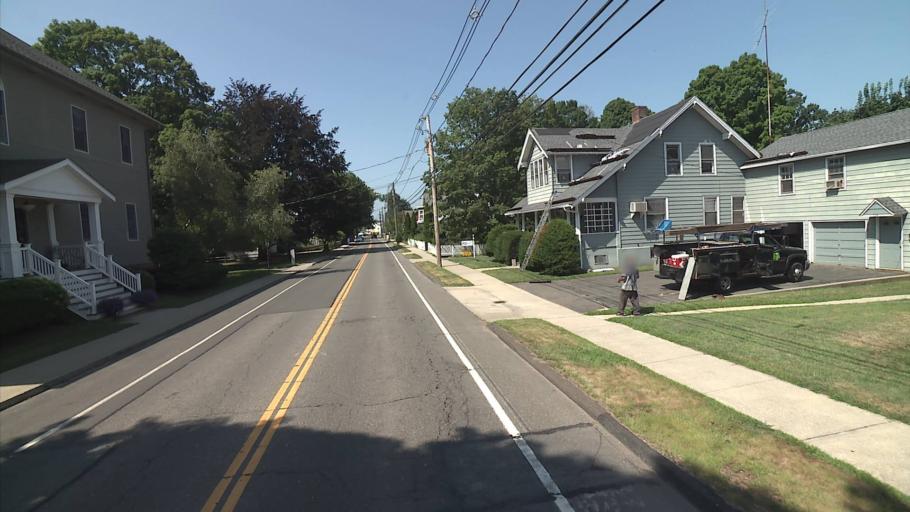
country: US
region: Connecticut
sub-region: New Haven County
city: Guilford Center
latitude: 41.2829
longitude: -72.6770
